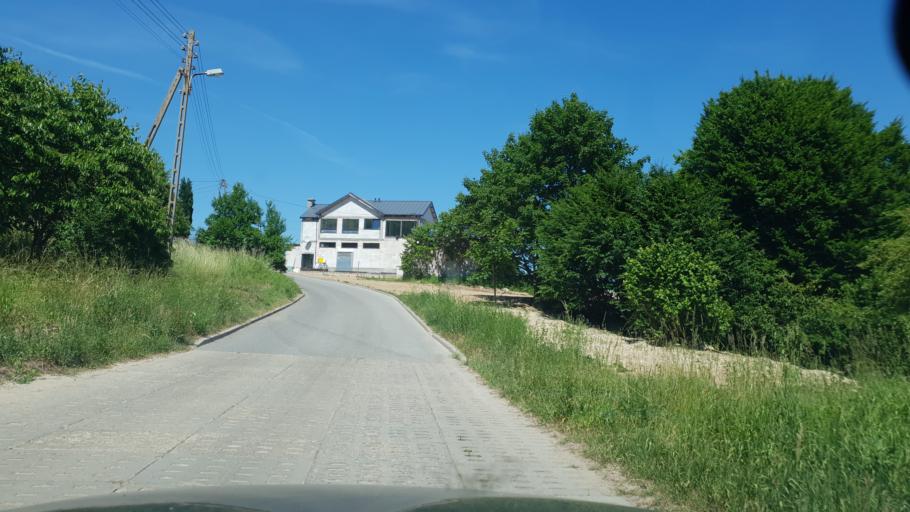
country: PL
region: Pomeranian Voivodeship
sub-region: Gdynia
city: Wielki Kack
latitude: 54.4596
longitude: 18.4860
